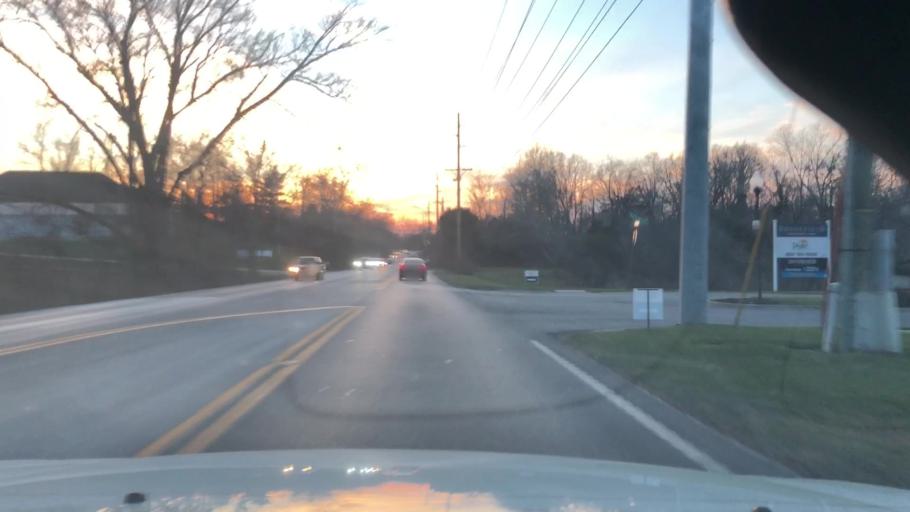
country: US
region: Kentucky
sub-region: Oldham County
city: Pewee Valley
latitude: 38.2346
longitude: -85.4495
